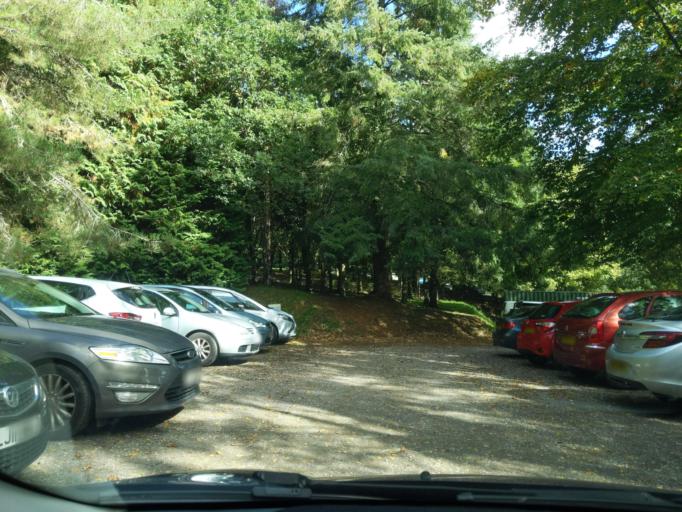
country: GB
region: England
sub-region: Devon
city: Bovey Tracey
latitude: 50.6316
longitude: -3.6477
